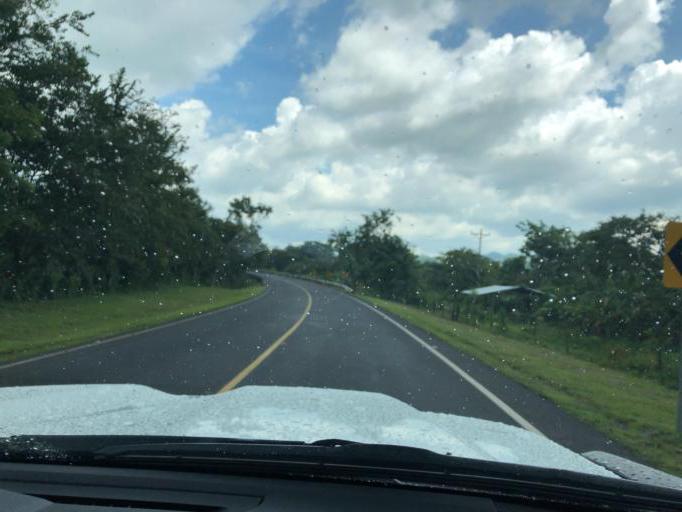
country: NI
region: Chontales
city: Villa Sandino
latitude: 12.0074
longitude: -84.9431
